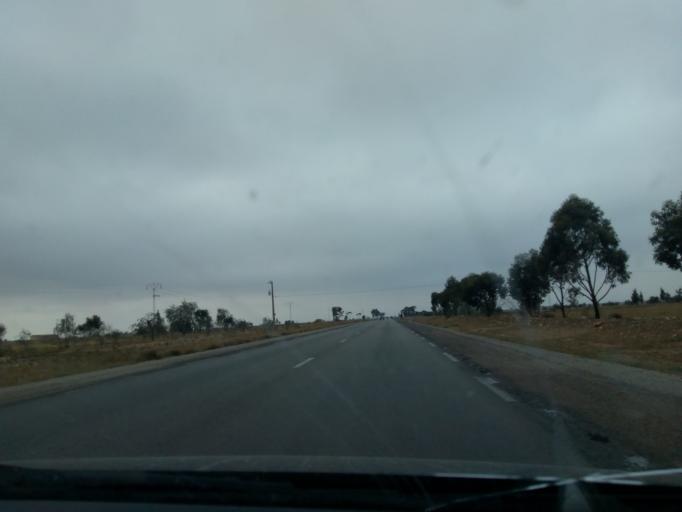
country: TN
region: Madanin
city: Medenine
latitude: 33.2775
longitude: 10.4690
